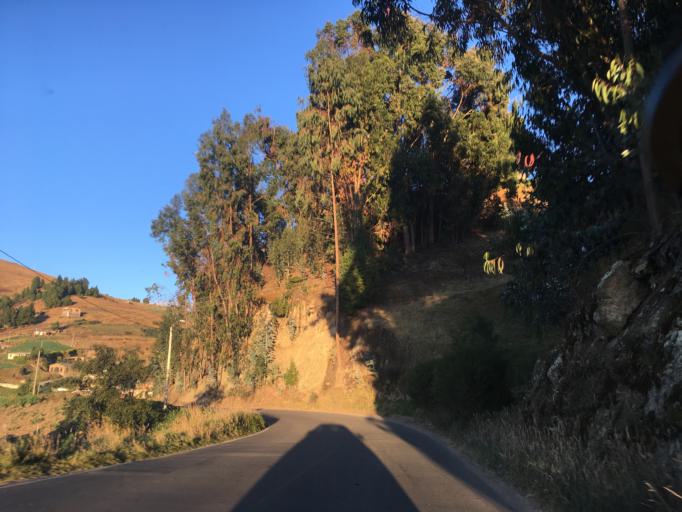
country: CO
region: Boyaca
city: Aquitania
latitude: 5.5381
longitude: -72.8838
